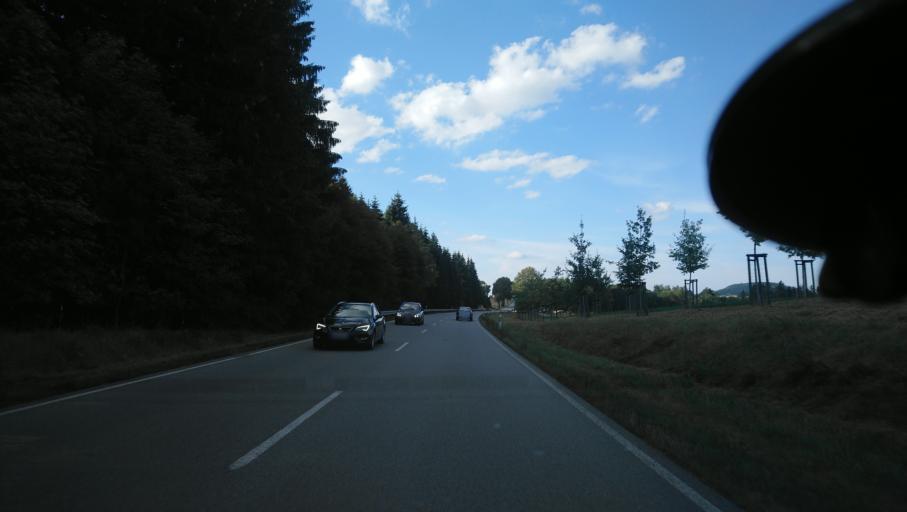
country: DE
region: Saxony
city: Konigswalde
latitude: 50.5343
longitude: 13.0251
